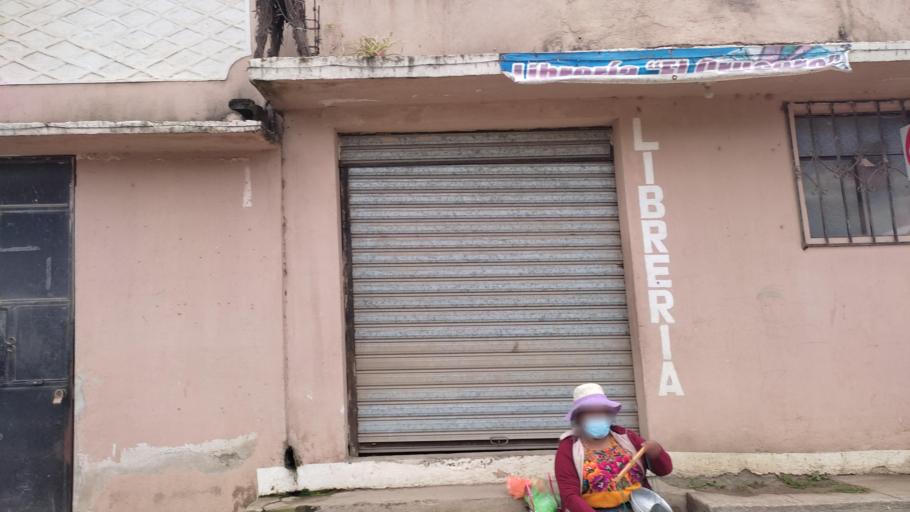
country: GT
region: Quetzaltenango
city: Quetzaltenango
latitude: 14.8560
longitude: -91.5286
